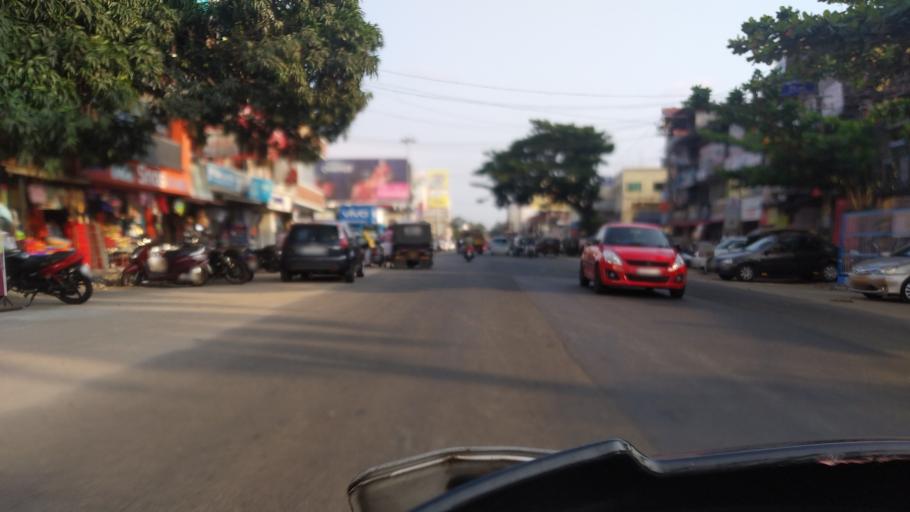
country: IN
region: Kerala
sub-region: Thrissur District
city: Thanniyam
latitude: 10.4155
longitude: 76.1069
